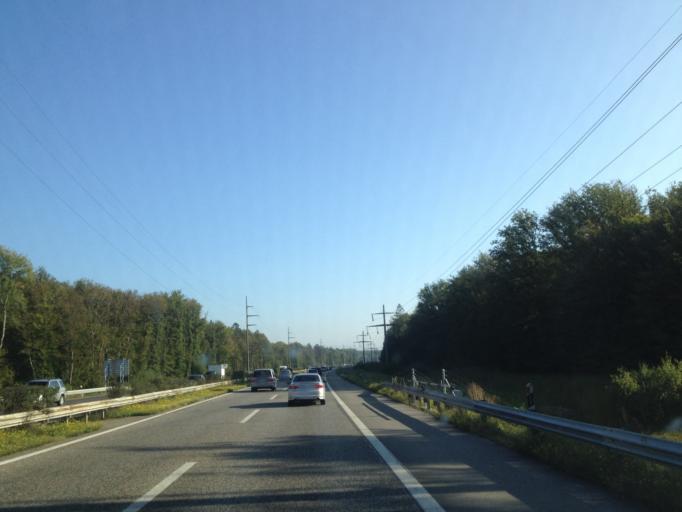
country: CH
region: Vaud
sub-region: Nyon District
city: Founex
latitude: 46.3517
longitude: 6.1732
